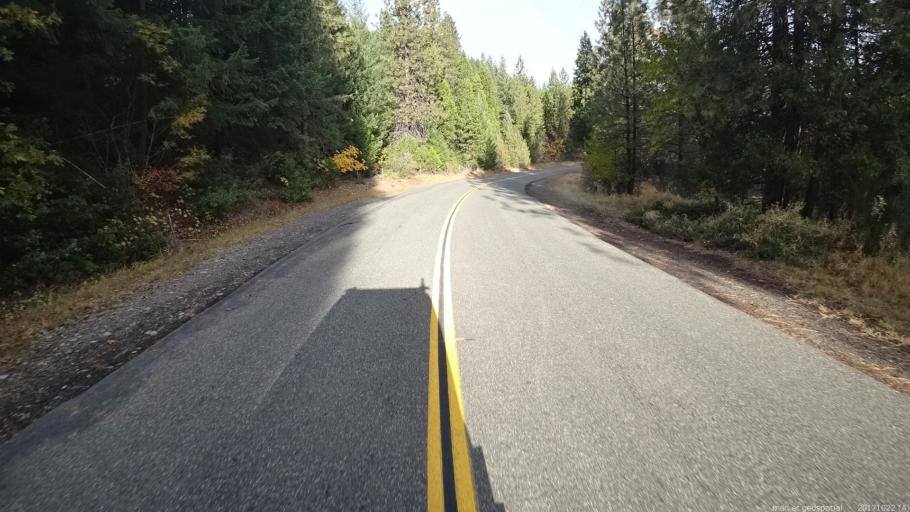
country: US
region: California
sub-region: Siskiyou County
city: Dunsmuir
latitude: 41.1548
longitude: -122.2932
